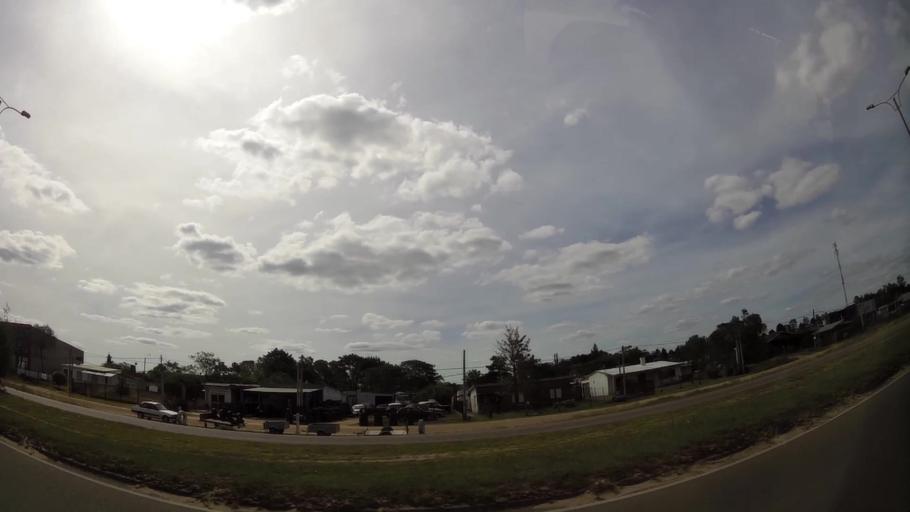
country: UY
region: Canelones
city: Pando
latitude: -34.8152
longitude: -55.9459
